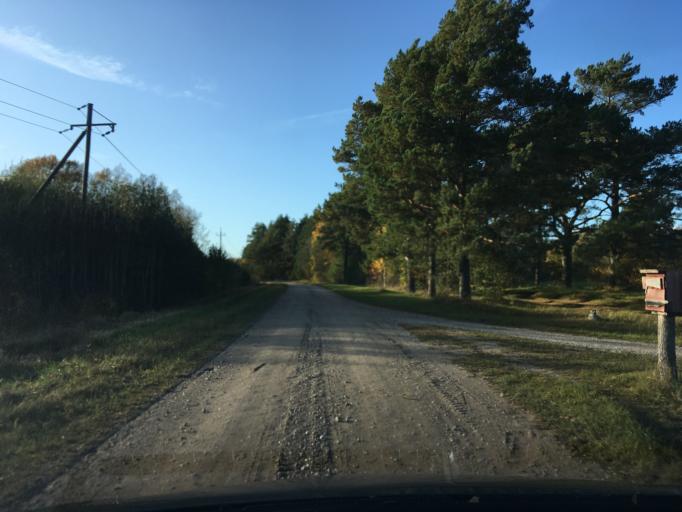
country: EE
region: Laeaene
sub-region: Lihula vald
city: Lihula
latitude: 58.5676
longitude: 23.7623
